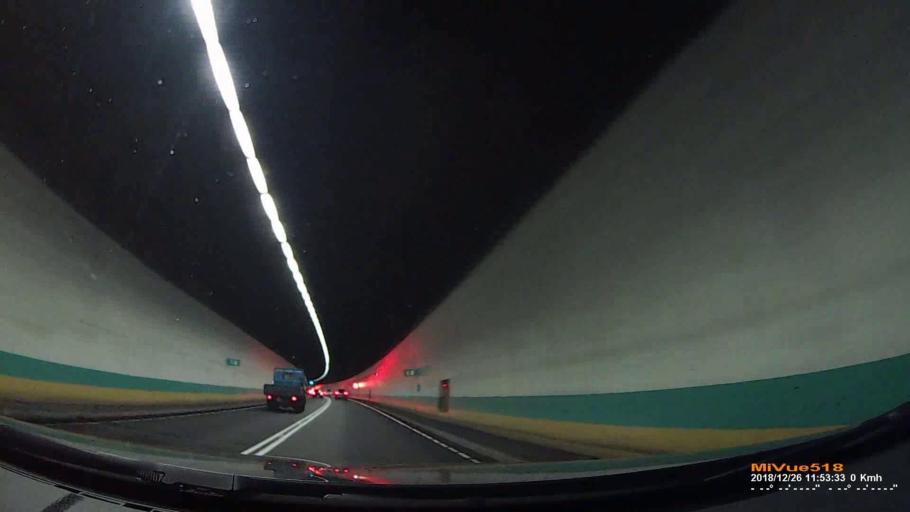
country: TW
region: Taiwan
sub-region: Keelung
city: Keelung
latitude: 24.9576
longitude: 121.6934
